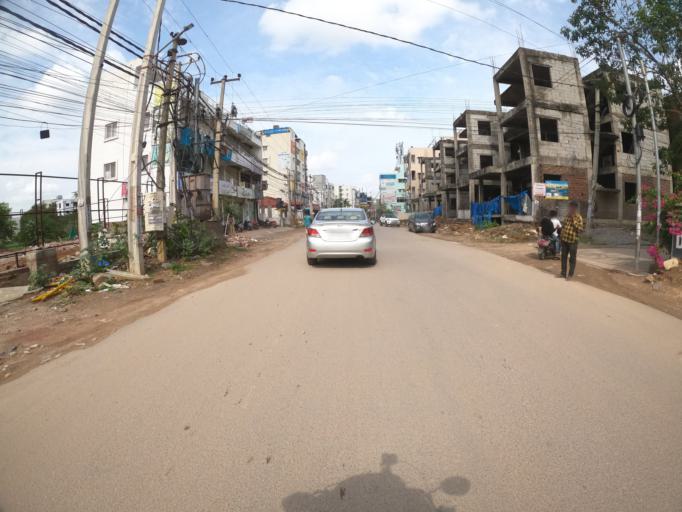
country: IN
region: Telangana
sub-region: Hyderabad
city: Hyderabad
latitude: 17.4078
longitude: 78.3810
